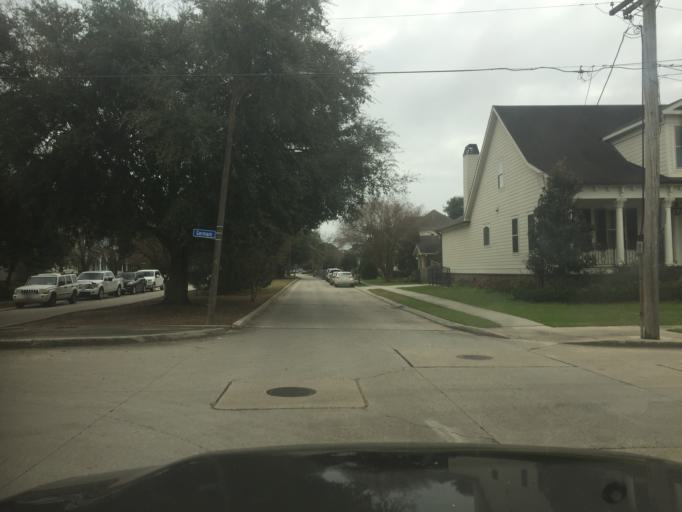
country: US
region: Louisiana
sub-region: Jefferson Parish
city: Metairie
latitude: 30.0007
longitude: -90.1032
